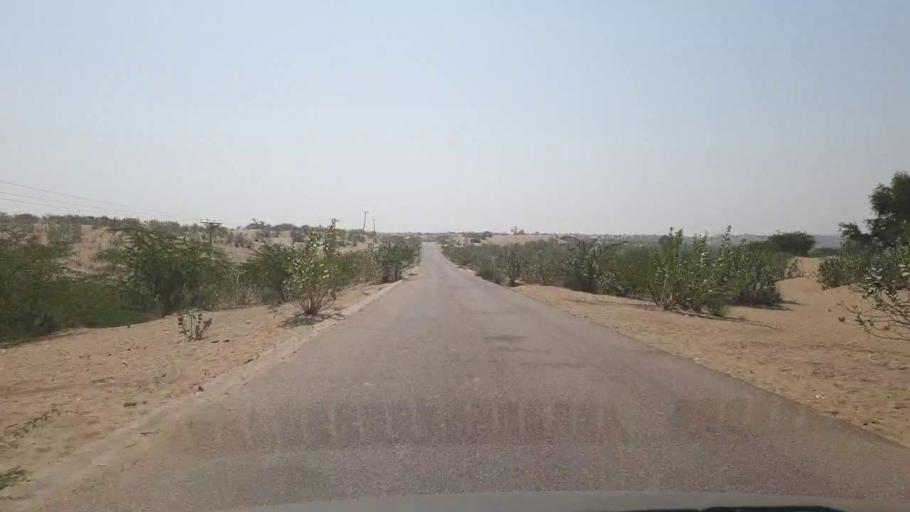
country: PK
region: Sindh
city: Chor
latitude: 25.6657
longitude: 70.1670
